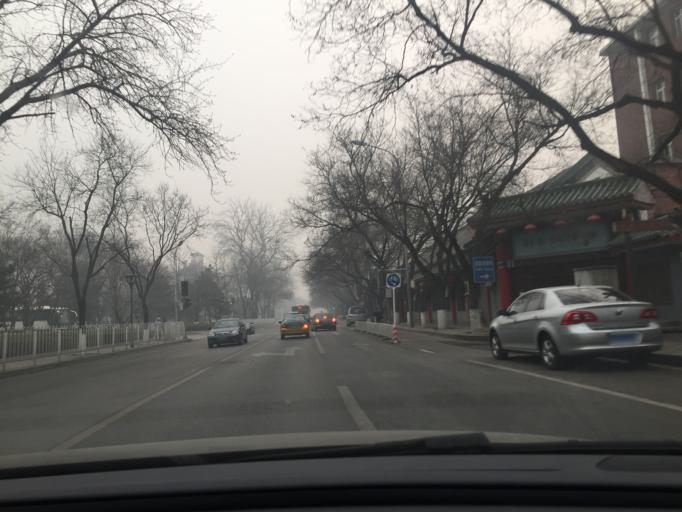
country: CN
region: Beijing
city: Beijing
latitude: 39.9122
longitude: 116.4005
